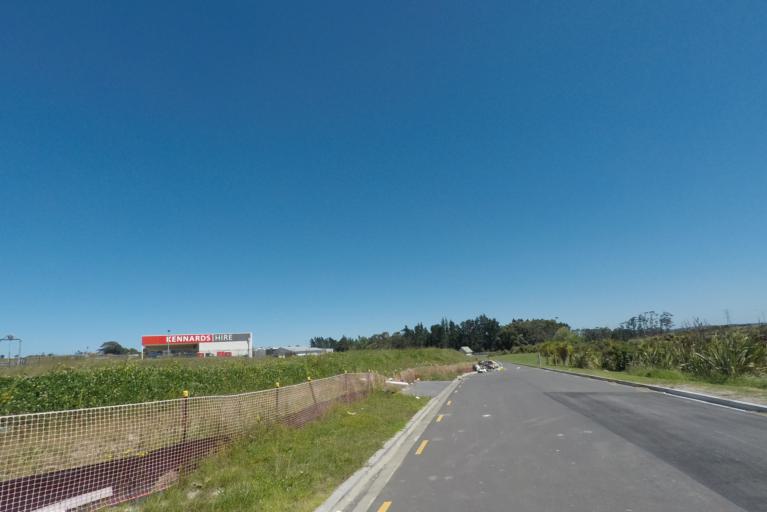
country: NZ
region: Auckland
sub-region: Auckland
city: Rosebank
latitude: -36.8080
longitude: 174.6063
